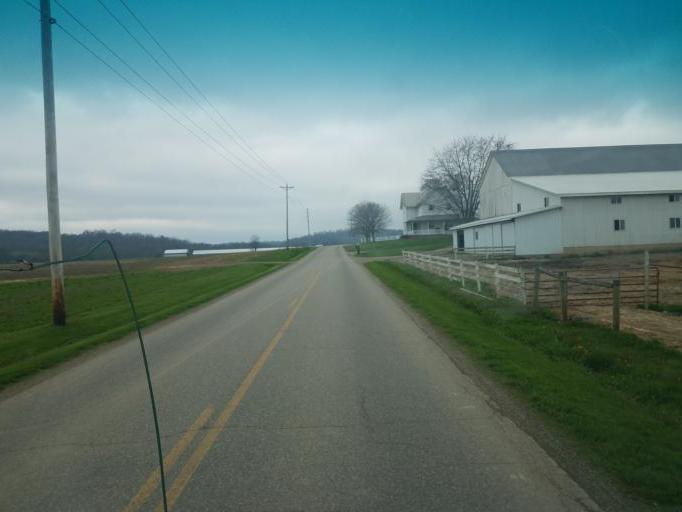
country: US
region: Ohio
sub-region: Stark County
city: Beach City
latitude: 40.6018
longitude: -81.6511
